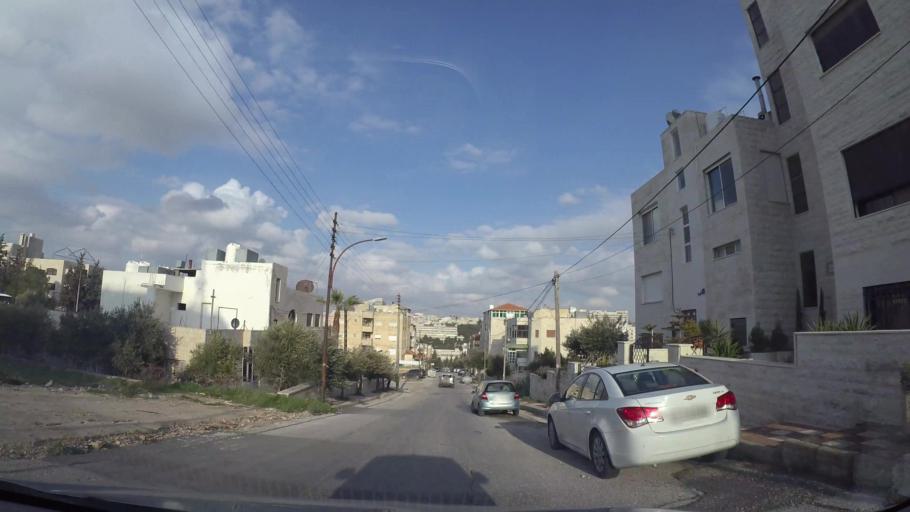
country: JO
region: Amman
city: Al Jubayhah
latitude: 32.0078
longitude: 35.8680
